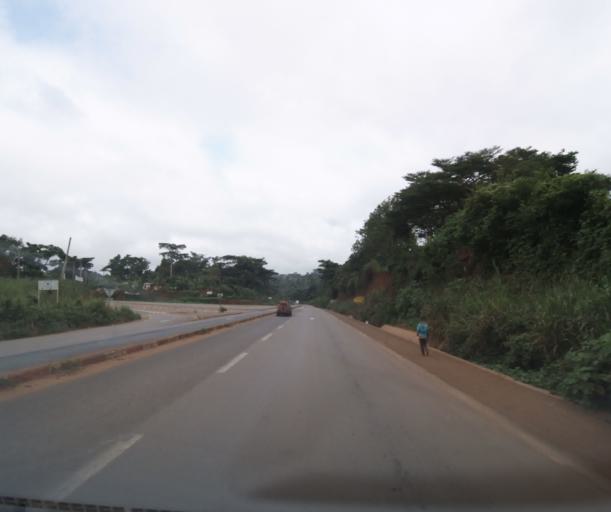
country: CM
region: Centre
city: Mbankomo
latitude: 3.7894
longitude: 11.4216
